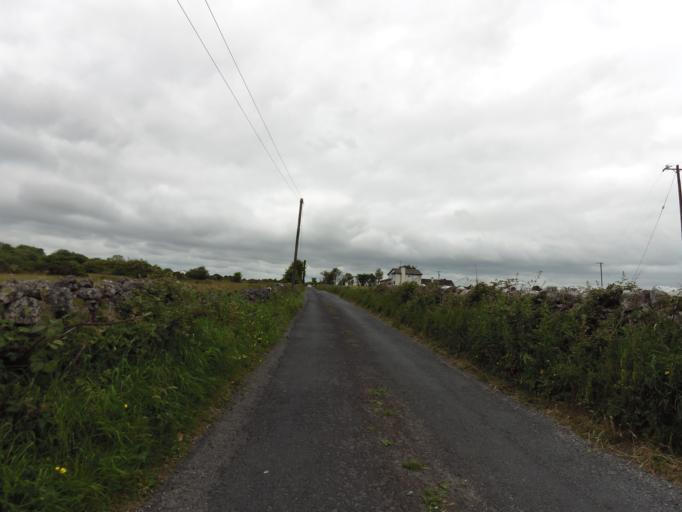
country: IE
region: Connaught
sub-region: County Galway
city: Athenry
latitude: 53.3153
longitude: -8.7355
